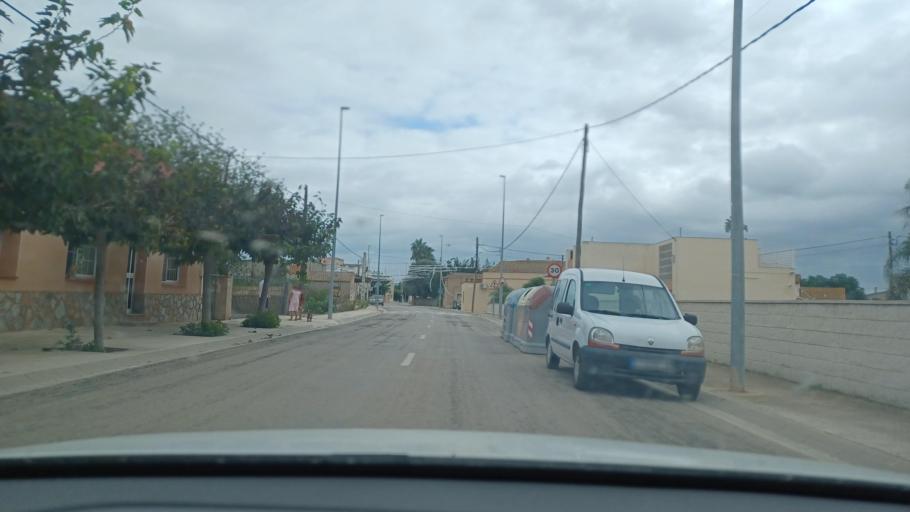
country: ES
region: Catalonia
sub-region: Provincia de Tarragona
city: Deltebre
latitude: 40.7251
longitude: 0.6895
